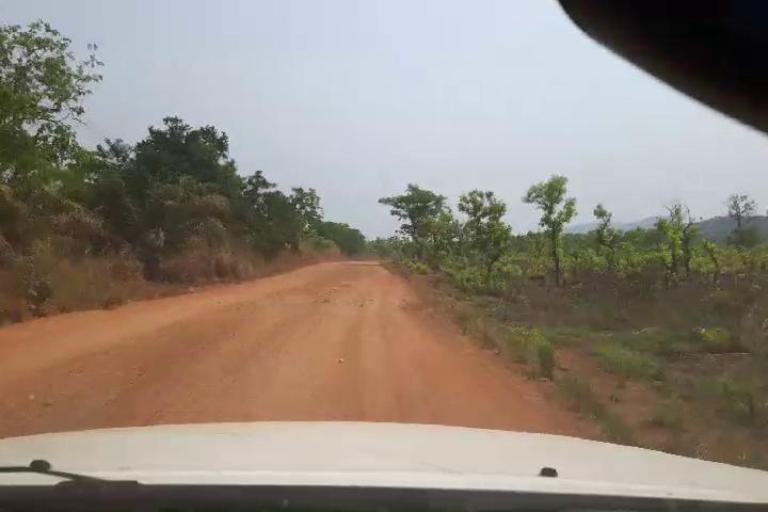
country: SL
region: Northern Province
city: Bumbuna
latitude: 8.9356
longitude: -11.8171
